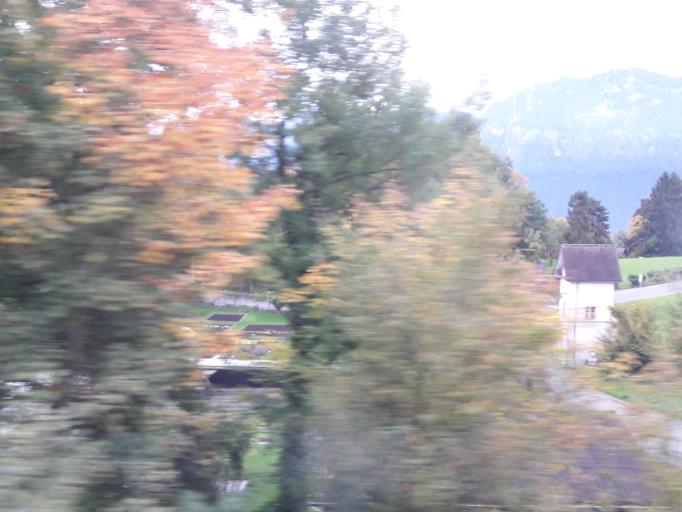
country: CH
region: Lucerne
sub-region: Lucerne-Land District
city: Meggen
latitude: 47.0424
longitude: 8.3699
